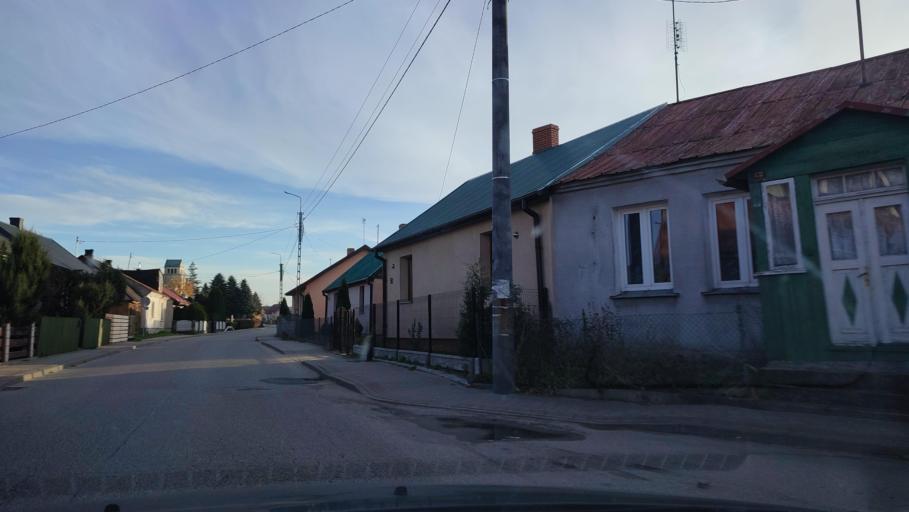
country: PL
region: Masovian Voivodeship
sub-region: Powiat mlawski
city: Dzierzgowo
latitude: 53.3152
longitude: 20.6732
